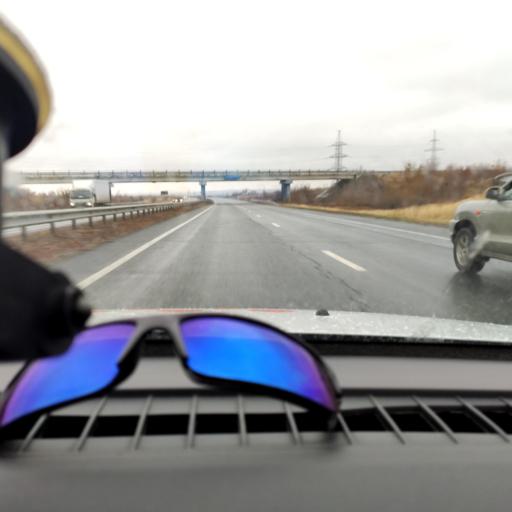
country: RU
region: Samara
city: Novokuybyshevsk
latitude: 53.0086
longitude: 49.9744
